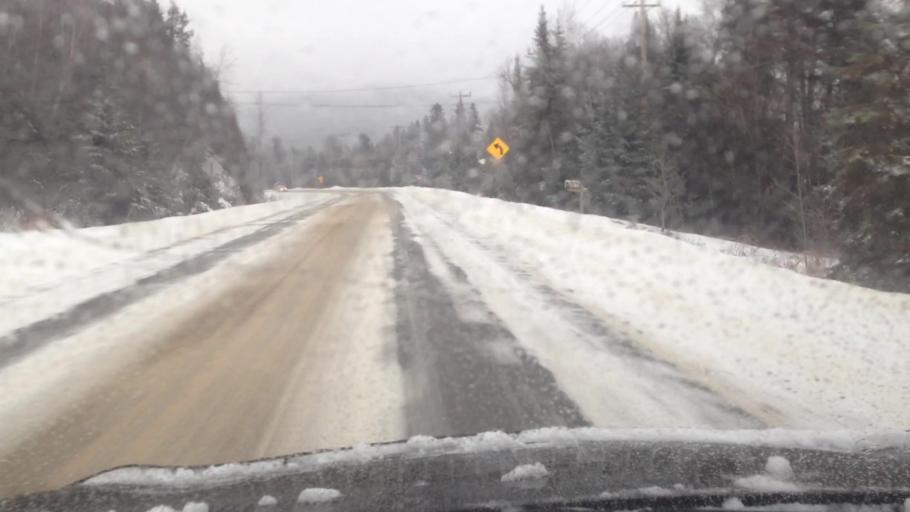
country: CA
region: Quebec
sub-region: Laurentides
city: Mont-Tremblant
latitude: 46.0884
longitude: -74.6092
